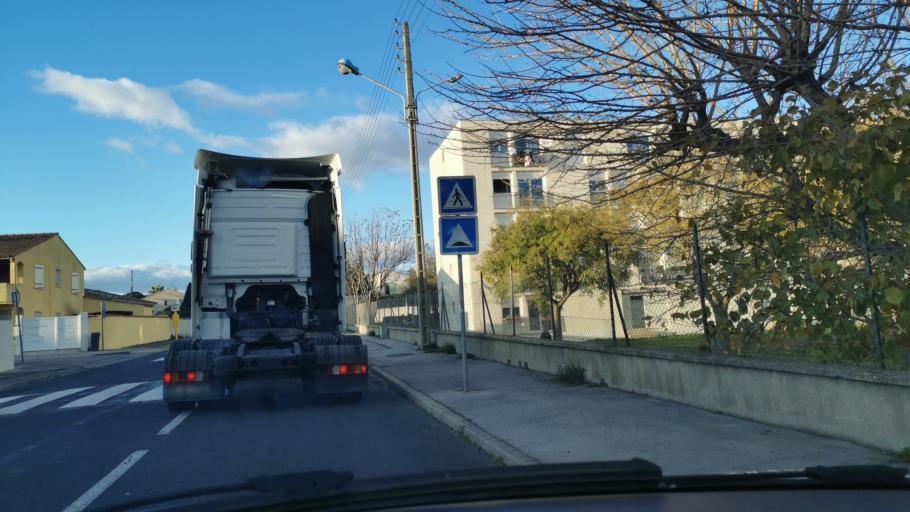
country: FR
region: Languedoc-Roussillon
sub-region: Departement de l'Herault
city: Frontignan
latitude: 43.4295
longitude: 3.7256
